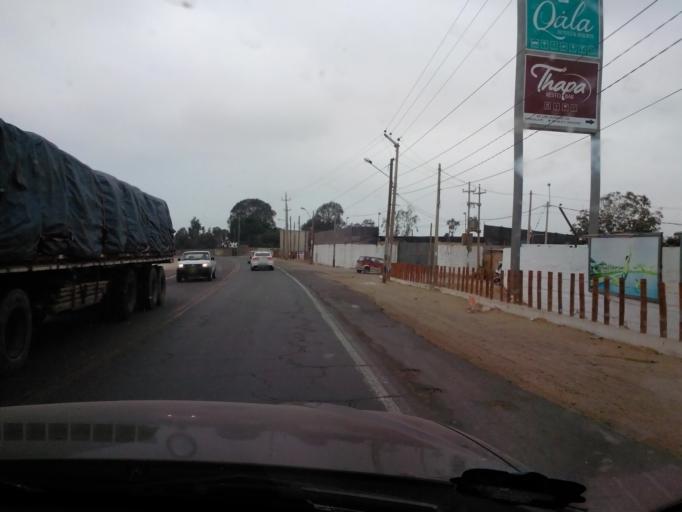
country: PE
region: Ica
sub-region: Provincia de Chincha
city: San Pedro
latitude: -13.4095
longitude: -76.1672
